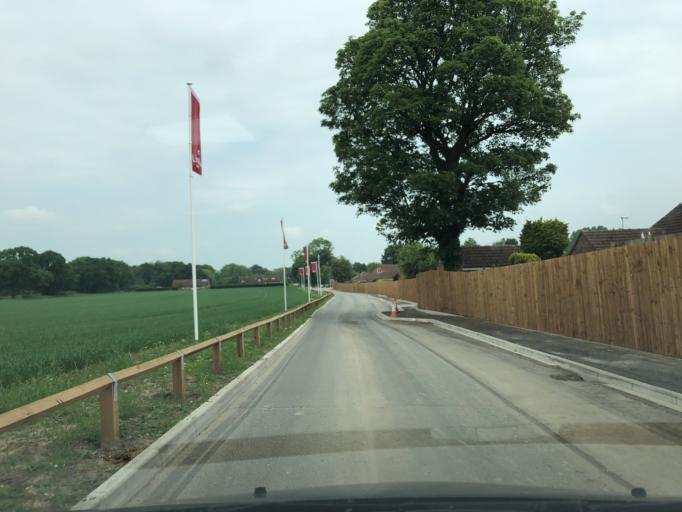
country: GB
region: England
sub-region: North Yorkshire
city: Boroughbridge
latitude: 54.0944
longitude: -1.4025
